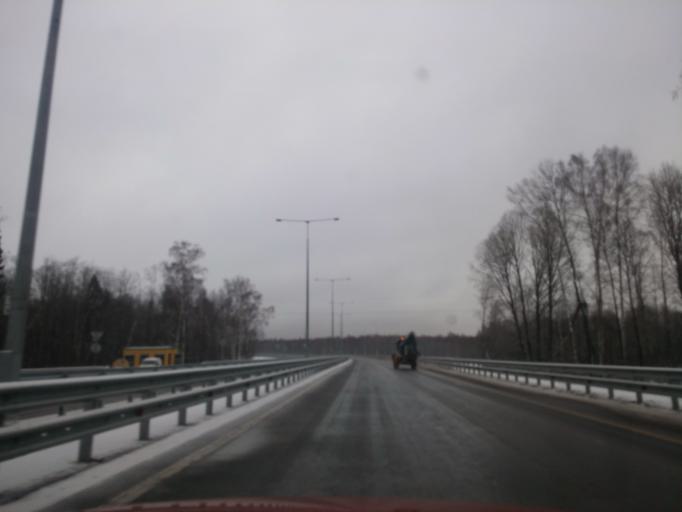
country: RU
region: Tverskaya
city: Likhoslavl'
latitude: 56.9615
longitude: 35.4790
